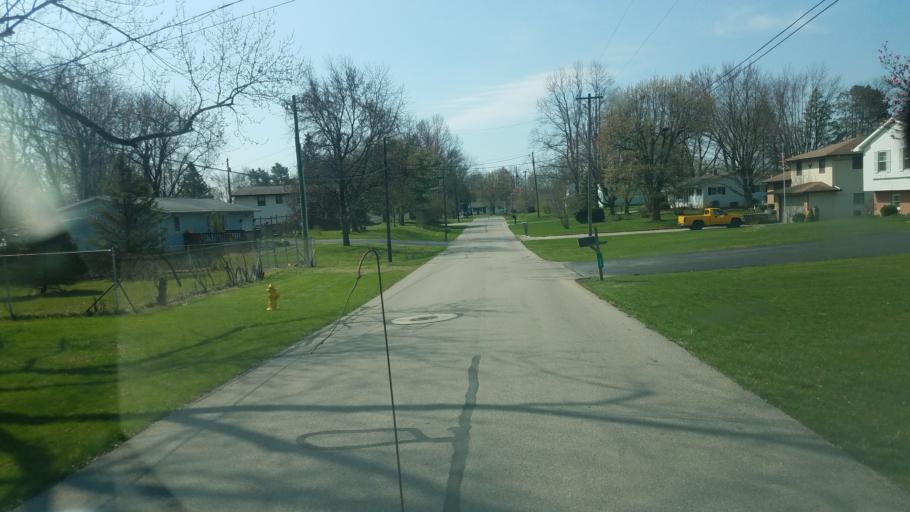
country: US
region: Ohio
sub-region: Delaware County
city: Delaware
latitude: 40.2836
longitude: -83.0740
